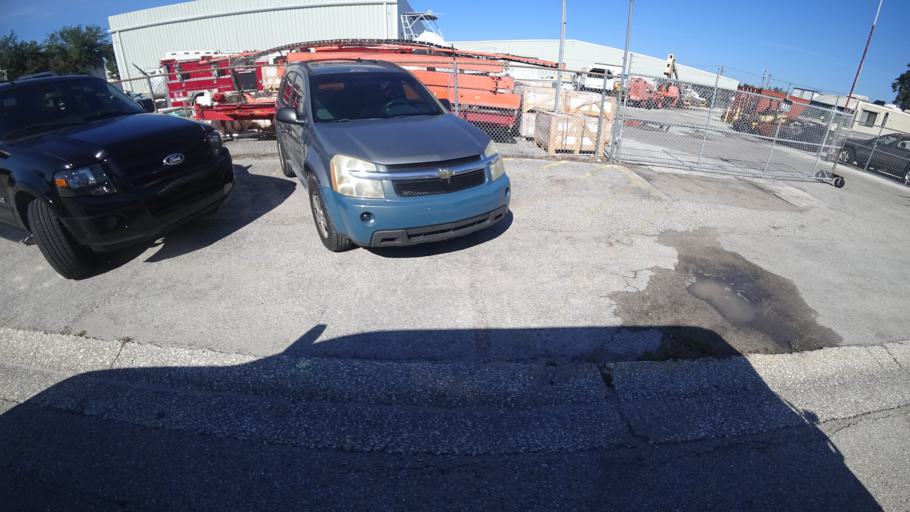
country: US
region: Florida
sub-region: Manatee County
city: Whitfield
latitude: 27.4140
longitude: -82.5385
